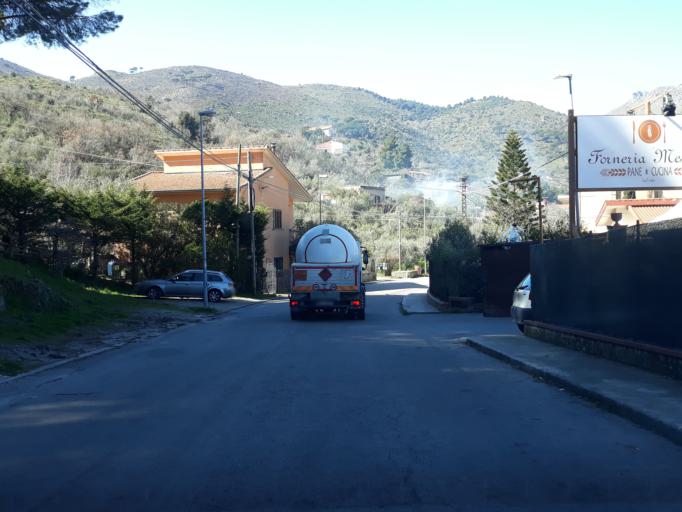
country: IT
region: Sicily
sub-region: Palermo
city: Piano dei Geli
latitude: 38.0851
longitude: 13.2653
